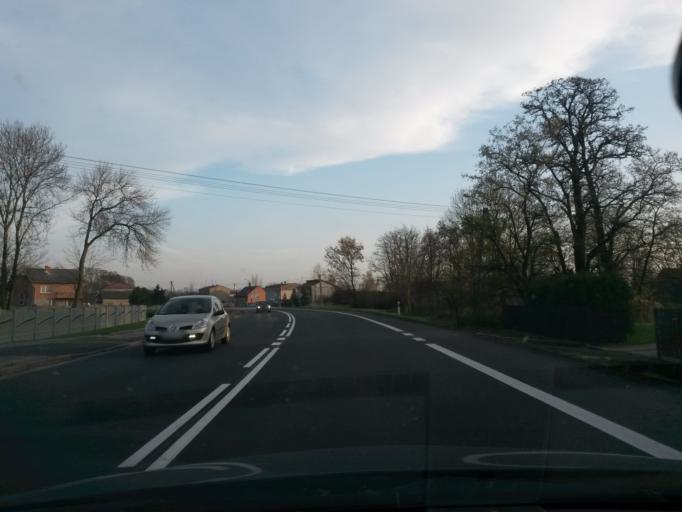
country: PL
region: Lodz Voivodeship
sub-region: Powiat wieruszowski
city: Walichnowy
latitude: 51.2698
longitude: 18.4363
